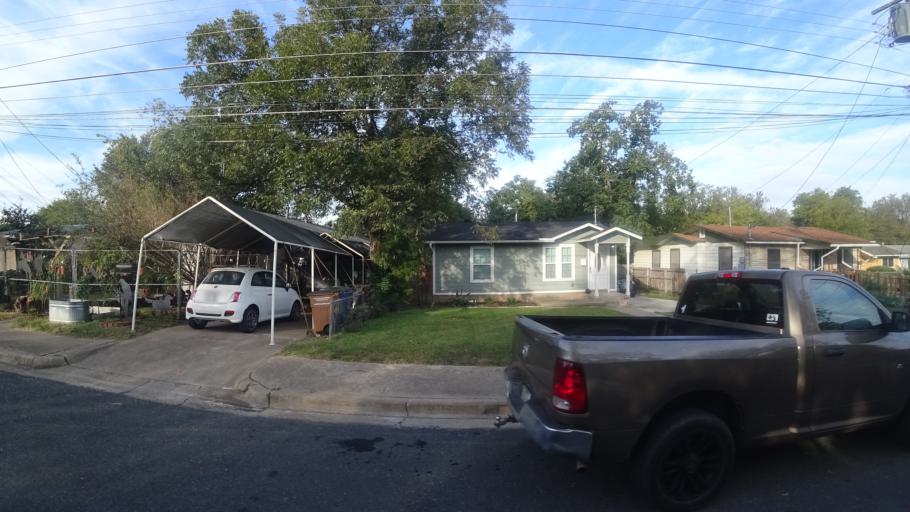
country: US
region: Texas
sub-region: Travis County
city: Austin
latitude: 30.2737
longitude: -97.7103
